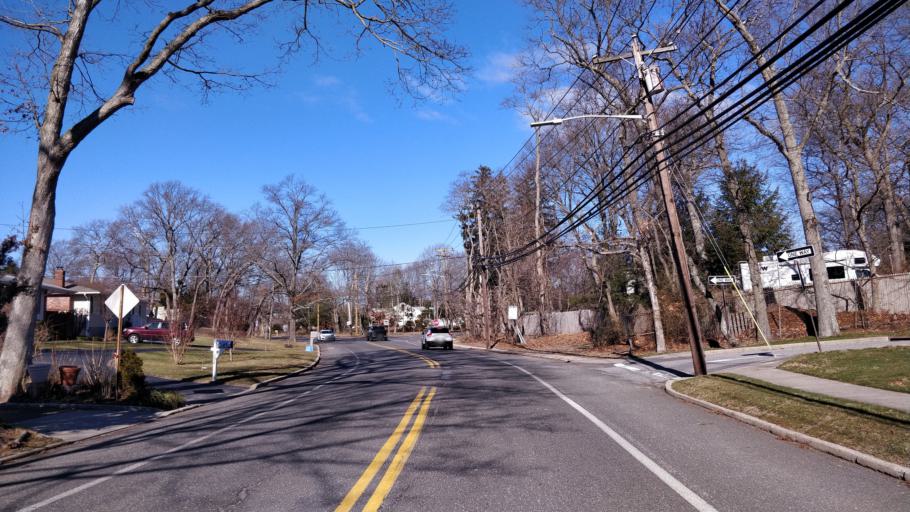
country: US
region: New York
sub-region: Suffolk County
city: Saint James
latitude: 40.8807
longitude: -73.1440
